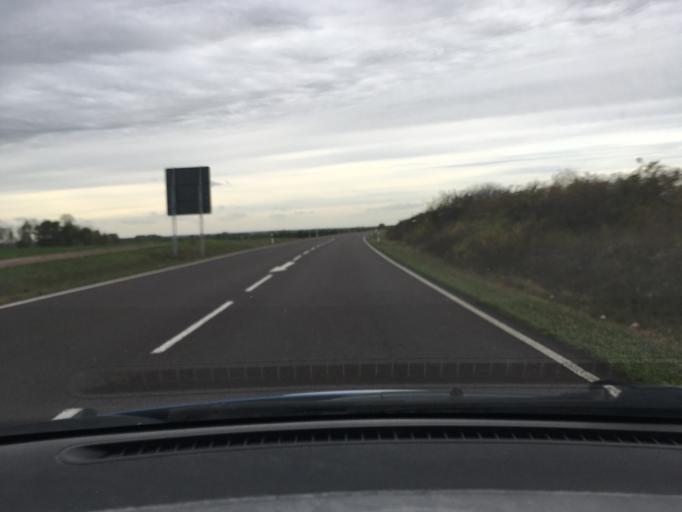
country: DE
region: Saxony-Anhalt
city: Leitzkau
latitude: 52.0507
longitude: 11.9469
